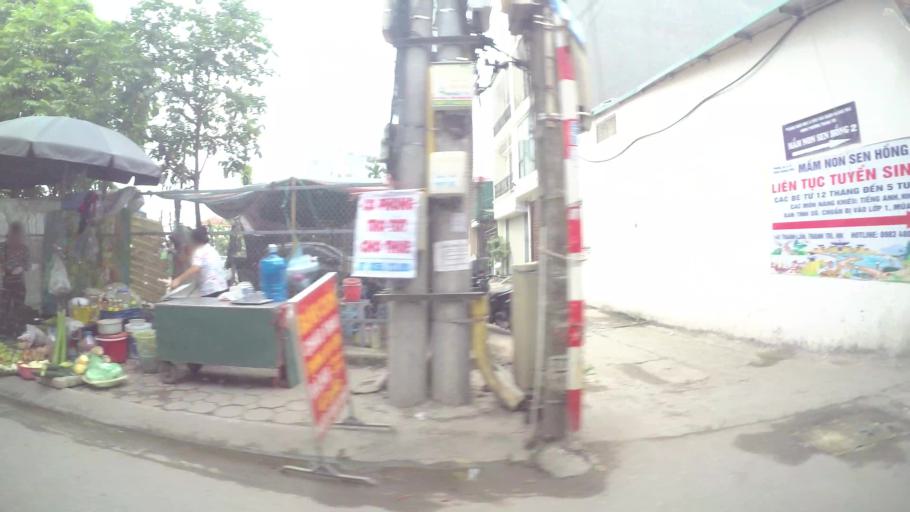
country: VN
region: Ha Noi
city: Hai BaTrung
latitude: 20.9886
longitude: 105.8885
